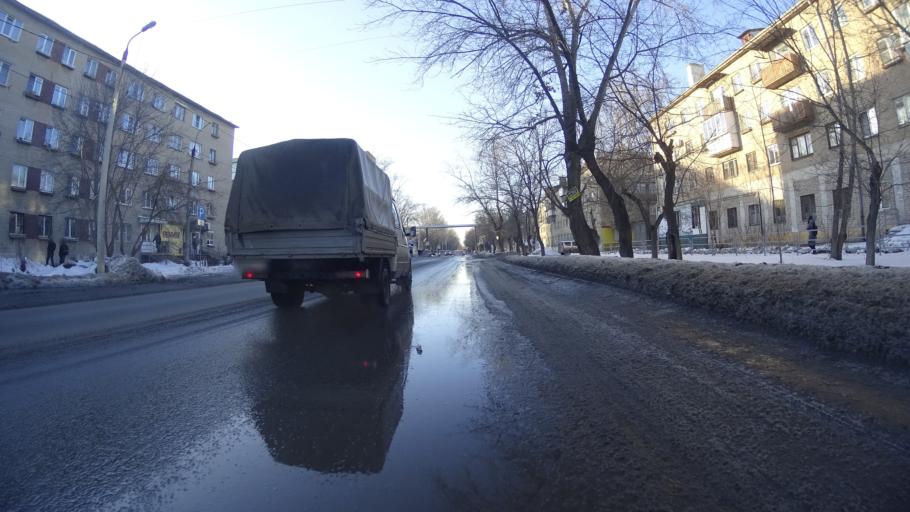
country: RU
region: Chelyabinsk
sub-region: Gorod Chelyabinsk
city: Chelyabinsk
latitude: 55.1266
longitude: 61.4724
